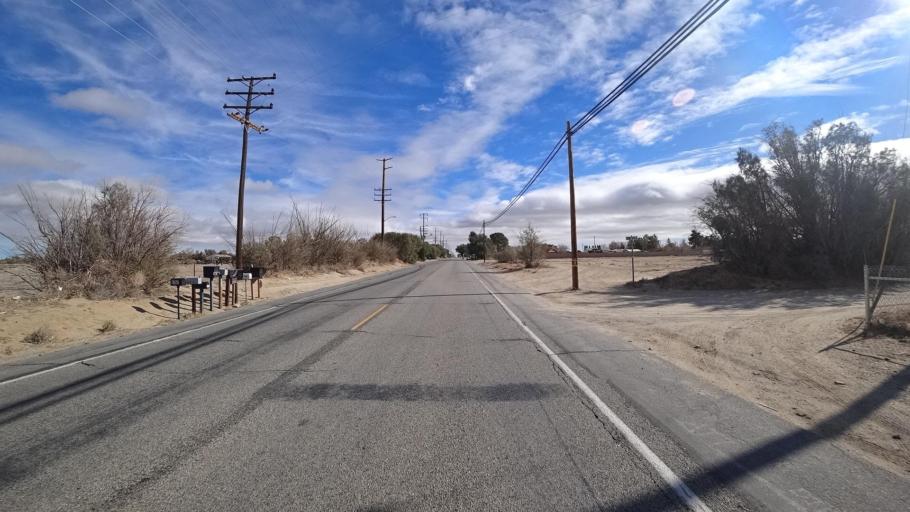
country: US
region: California
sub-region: Kern County
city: Rosamond
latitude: 34.8638
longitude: -118.2339
